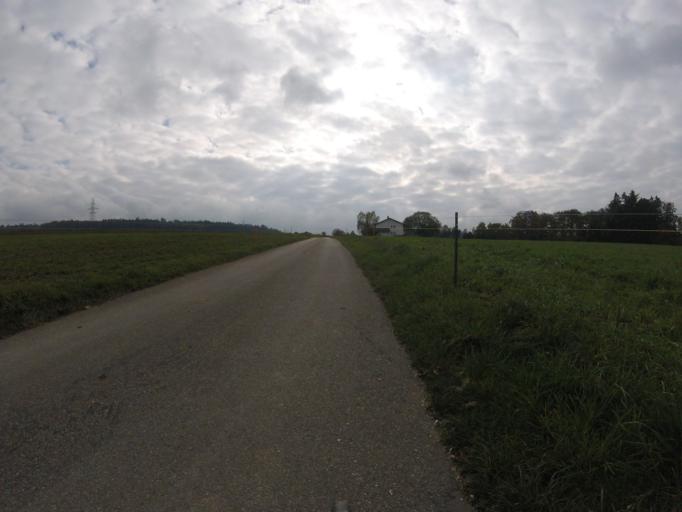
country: CH
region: Fribourg
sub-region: Sense District
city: Flamatt
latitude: 46.9102
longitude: 7.3662
